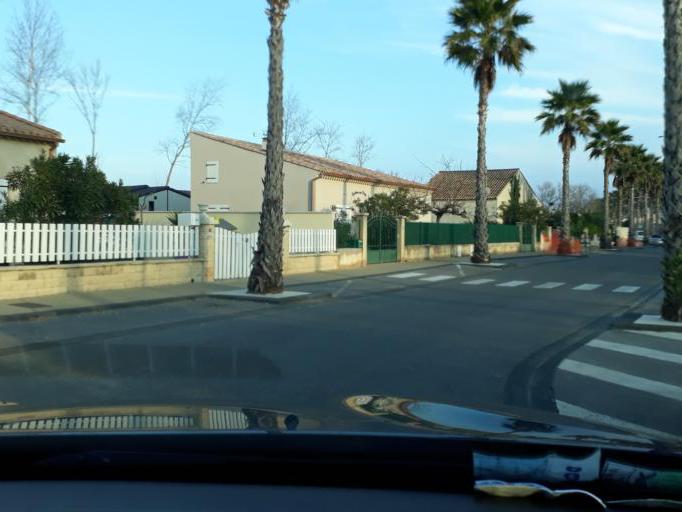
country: FR
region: Languedoc-Roussillon
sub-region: Departement de l'Herault
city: Marseillan
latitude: 43.3180
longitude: 3.5473
